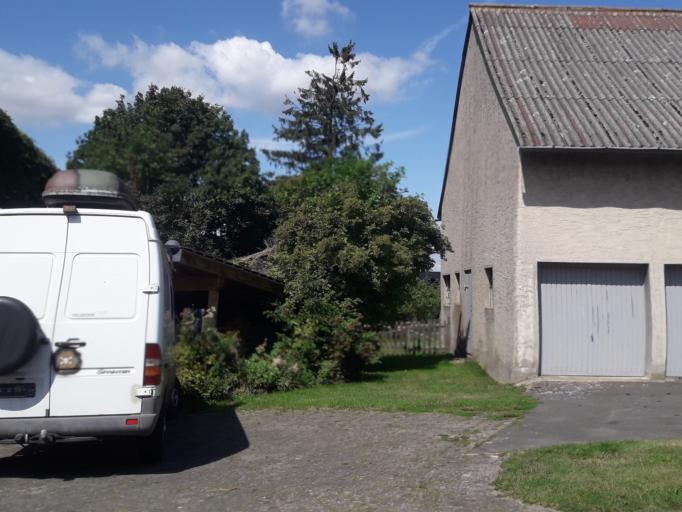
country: DE
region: North Rhine-Westphalia
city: Lichtenau
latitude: 51.6549
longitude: 8.8404
